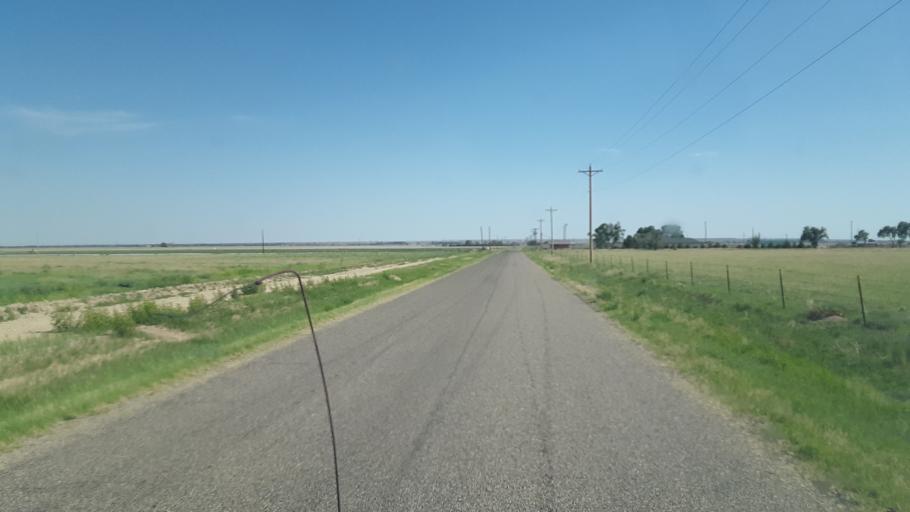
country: US
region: Colorado
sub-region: Otero County
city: Fowler
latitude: 38.1657
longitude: -103.9314
